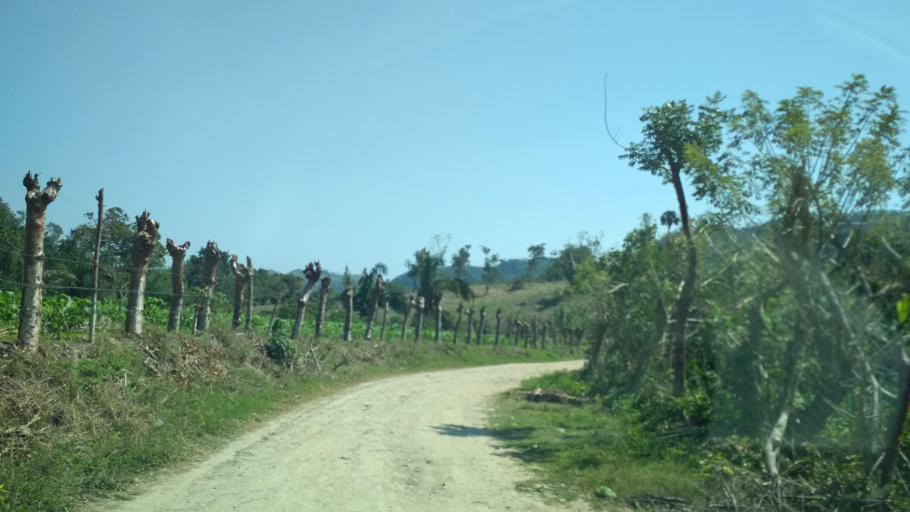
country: MX
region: Veracruz
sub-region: Papantla
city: Polutla
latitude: 20.4828
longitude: -97.2265
